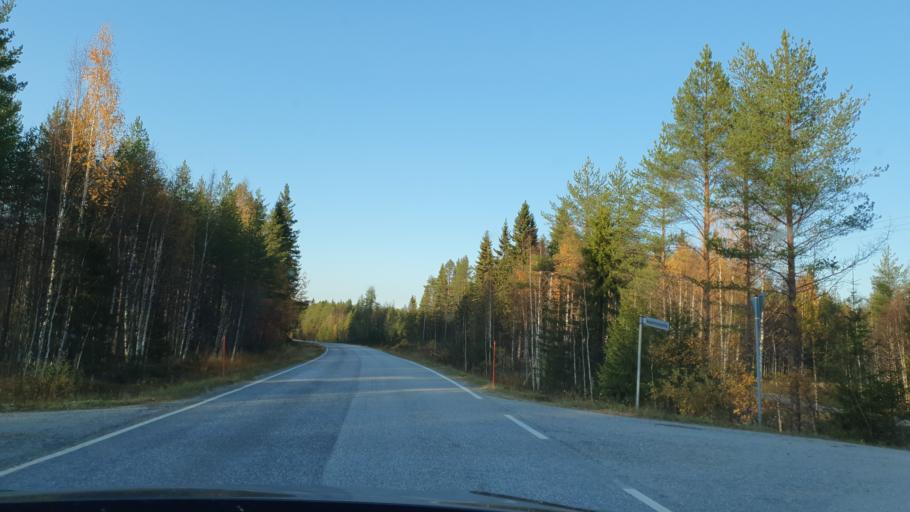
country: FI
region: Kainuu
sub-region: Kehys-Kainuu
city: Kuhmo
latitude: 64.3528
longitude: 29.4900
